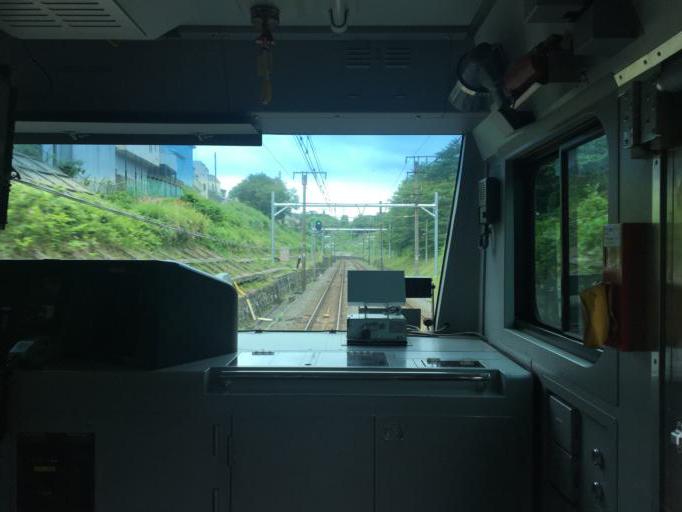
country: JP
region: Kanagawa
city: Yokohama
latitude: 35.4407
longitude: 139.5652
